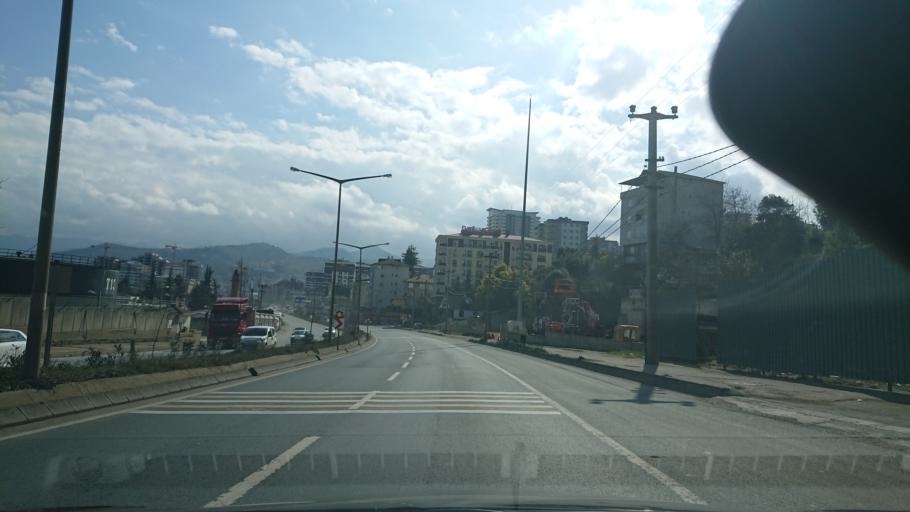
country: TR
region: Trabzon
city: Yomra
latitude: 40.9744
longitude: 39.8317
